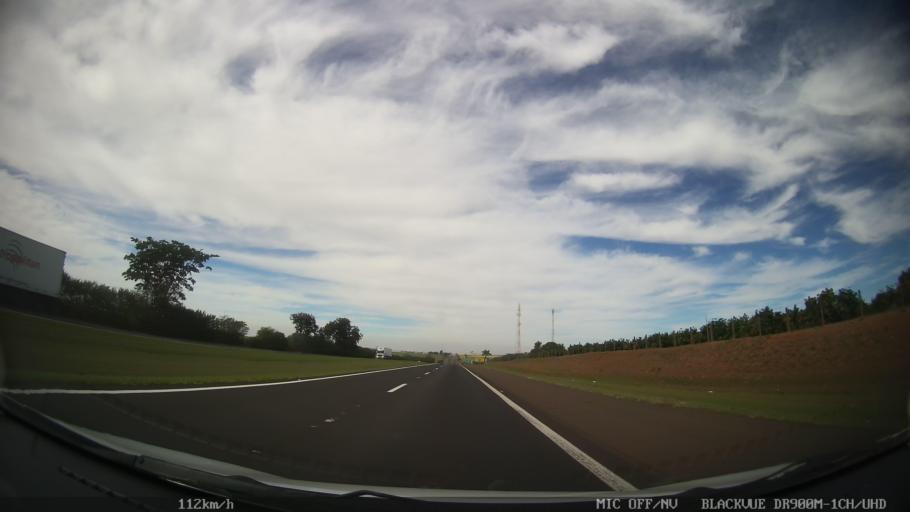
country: BR
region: Sao Paulo
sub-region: Taquaritinga
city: Taquaritinga
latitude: -21.4720
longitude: -48.6040
